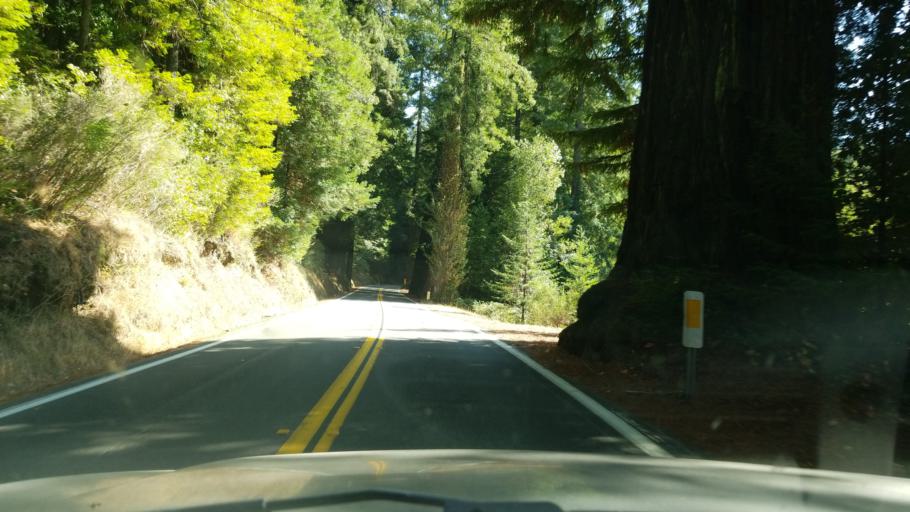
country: US
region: California
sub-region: Humboldt County
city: Redway
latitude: 40.2464
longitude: -123.8225
